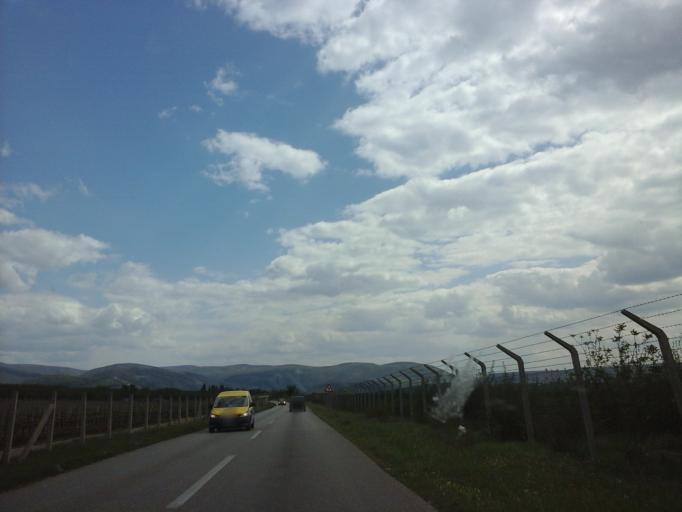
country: BA
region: Federation of Bosnia and Herzegovina
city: Blagaj
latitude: 43.2857
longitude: 17.8498
